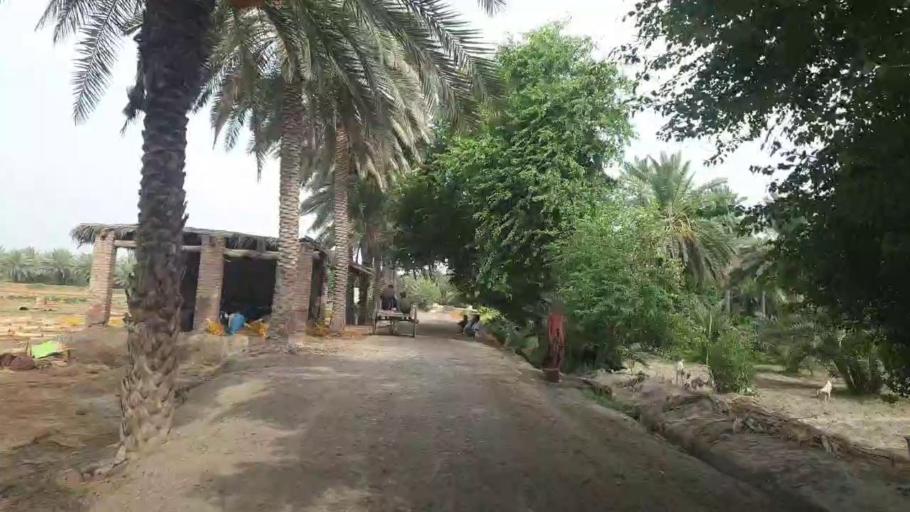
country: PK
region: Sindh
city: Sukkur
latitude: 27.6418
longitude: 68.8219
